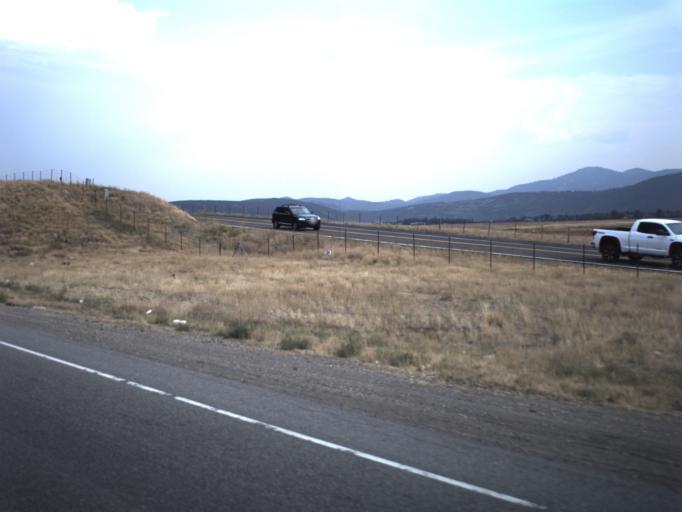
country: US
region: Utah
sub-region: Summit County
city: Snyderville
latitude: 40.7241
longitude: -111.5345
